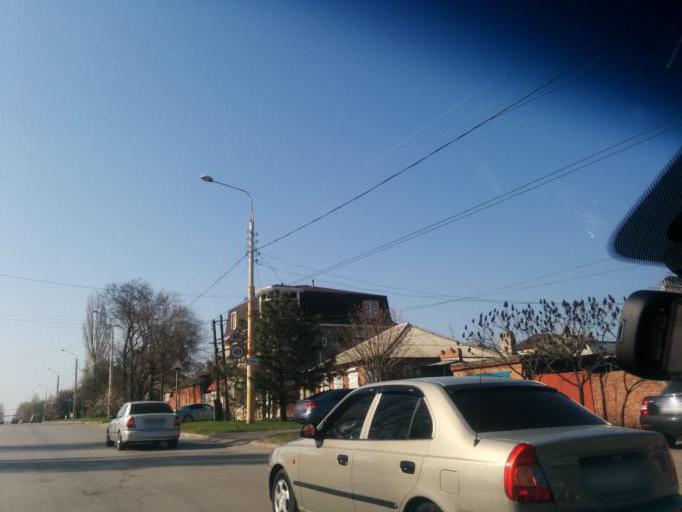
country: RU
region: Rostov
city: Shakhty
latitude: 47.7000
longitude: 40.2044
